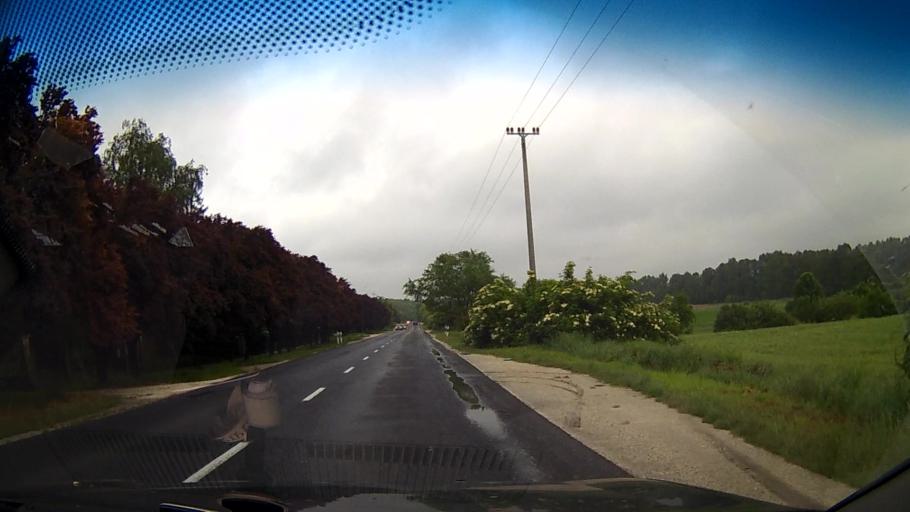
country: HU
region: Komarom-Esztergom
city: Piliscsev
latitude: 47.6533
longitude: 18.7950
